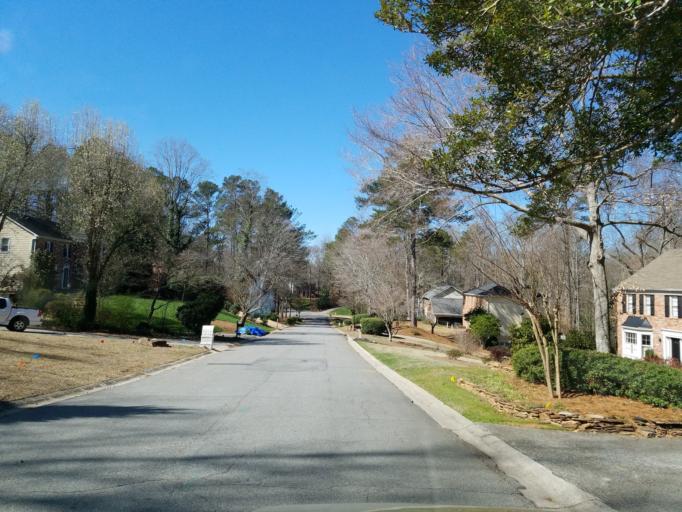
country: US
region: Georgia
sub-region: Fulton County
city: Sandy Springs
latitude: 33.9749
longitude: -84.4486
